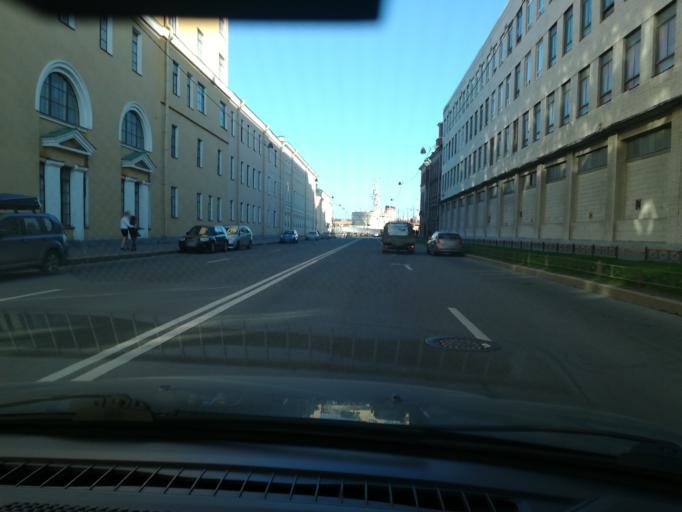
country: RU
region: St.-Petersburg
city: Vasyl'evsky Ostrov
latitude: 59.9301
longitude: 30.2662
